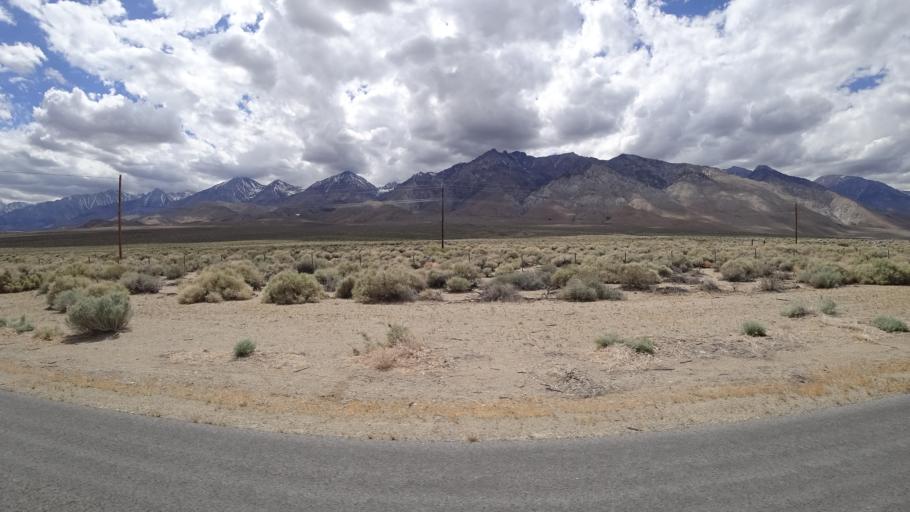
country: US
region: California
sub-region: Inyo County
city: Big Pine
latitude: 36.8766
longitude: -118.2388
